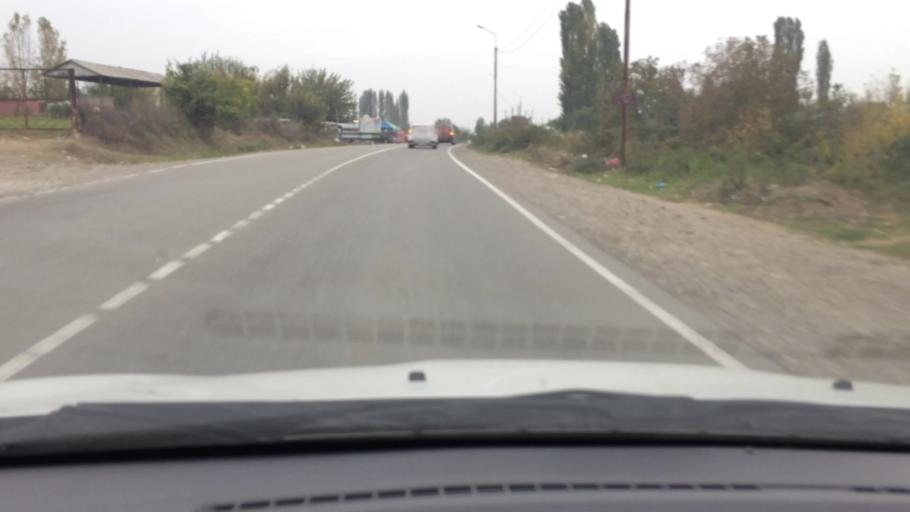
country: AM
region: Tavush
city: Bagratashen
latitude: 41.2520
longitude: 44.7996
